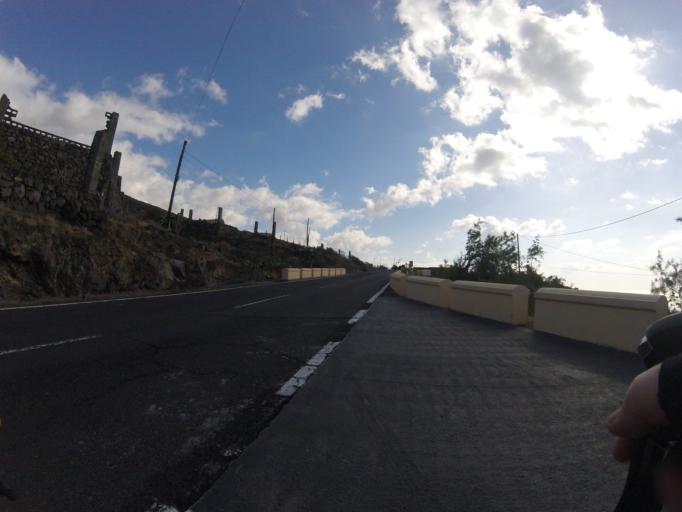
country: ES
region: Canary Islands
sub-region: Provincia de Santa Cruz de Tenerife
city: Candelaria
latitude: 28.3907
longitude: -16.3526
